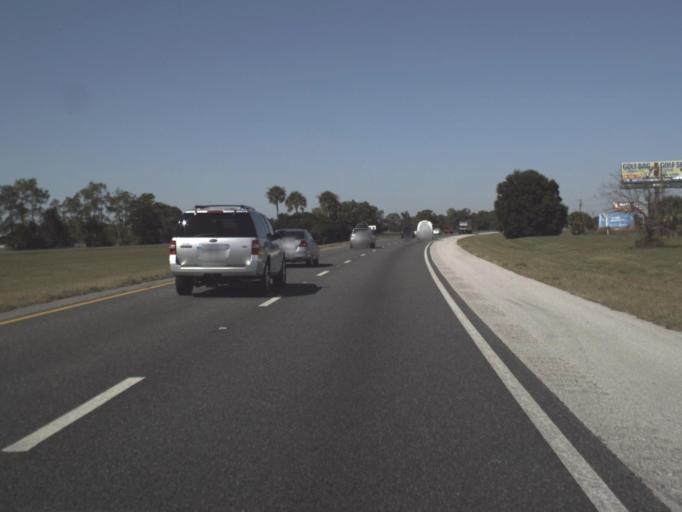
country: US
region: Florida
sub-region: Sumter County
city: Wildwood
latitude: 28.7909
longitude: -81.9890
